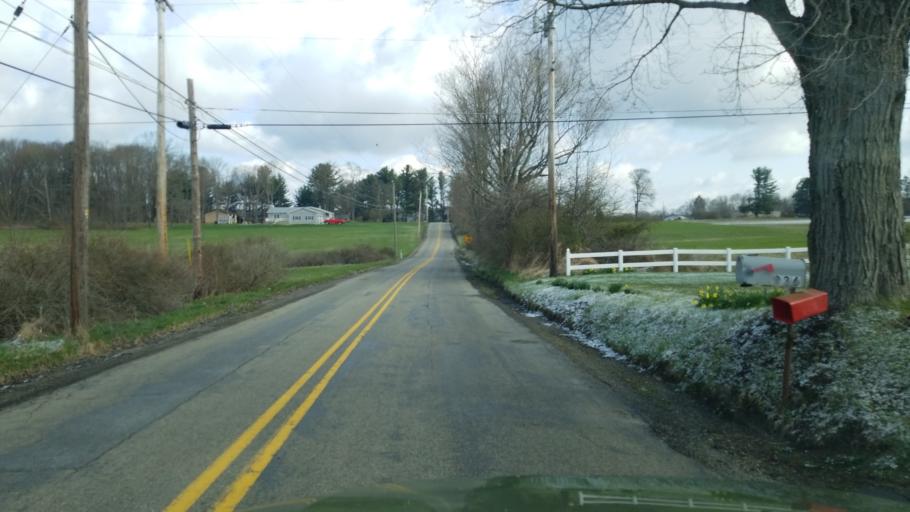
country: US
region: Pennsylvania
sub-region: Jefferson County
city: Brockway
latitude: 41.2726
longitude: -78.8430
